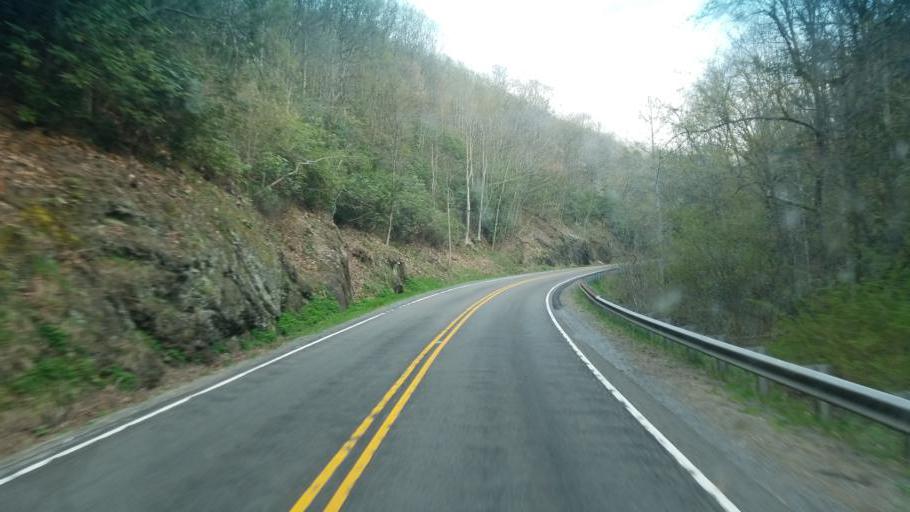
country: US
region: Virginia
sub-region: Smyth County
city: Atkins
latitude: 36.7995
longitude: -81.4035
